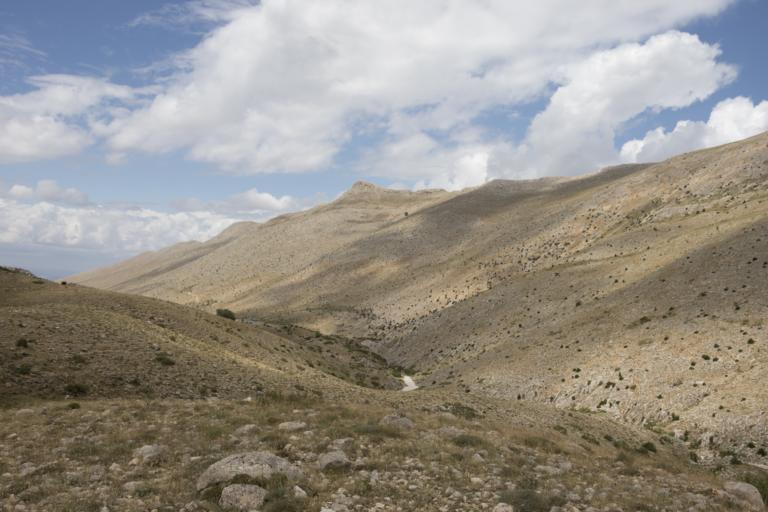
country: TR
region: Kayseri
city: Toklar
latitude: 38.4301
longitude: 36.1699
